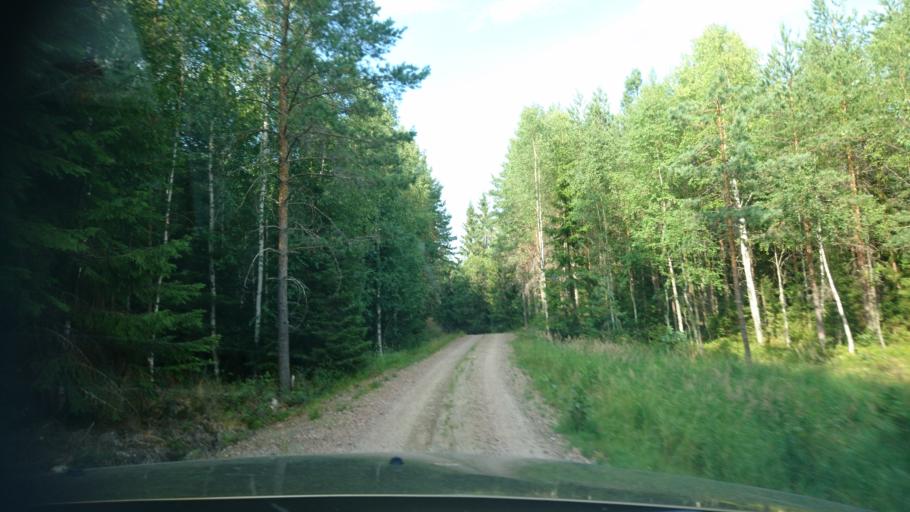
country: SE
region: Vaermland
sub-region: Kristinehamns Kommun
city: Bjorneborg
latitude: 59.3101
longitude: 14.3127
